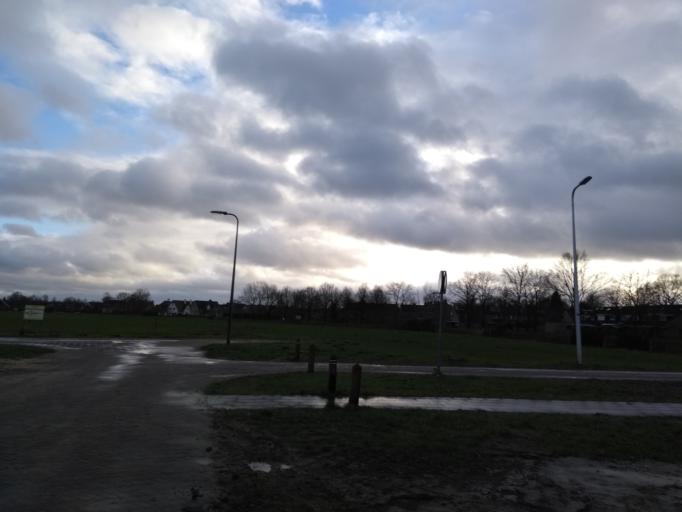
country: NL
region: Overijssel
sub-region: Gemeente Almelo
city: Almelo
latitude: 52.3788
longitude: 6.6919
